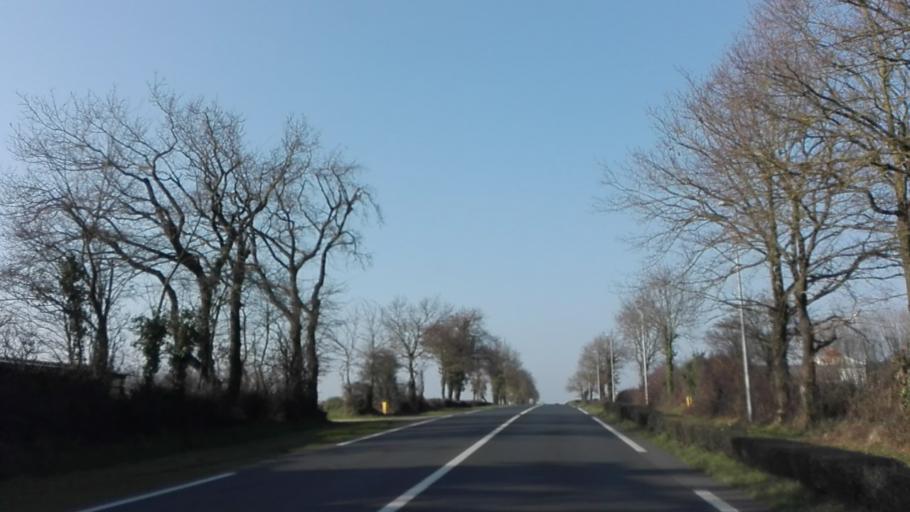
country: FR
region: Pays de la Loire
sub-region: Departement de la Vendee
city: Saint-Georges-de-Montaigu
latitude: 46.9535
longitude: -1.3046
